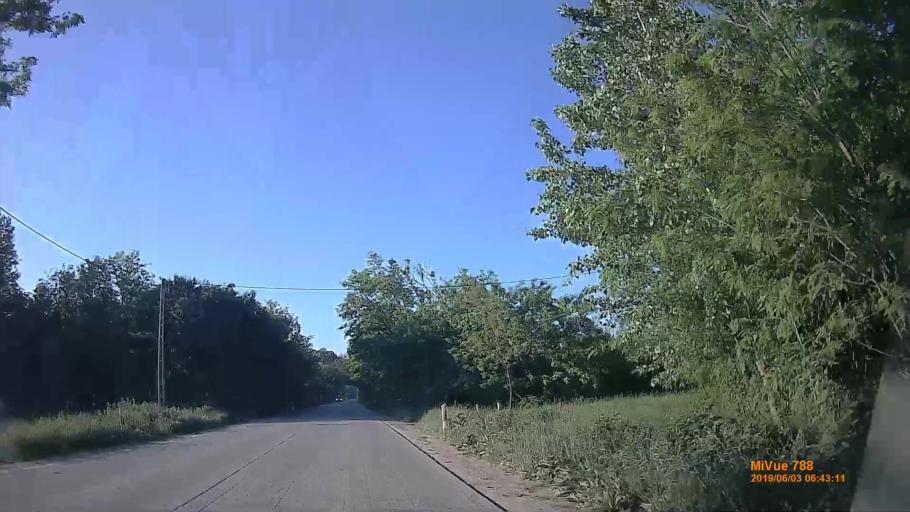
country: HU
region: Pest
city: Delegyhaza
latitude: 47.2582
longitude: 19.1223
